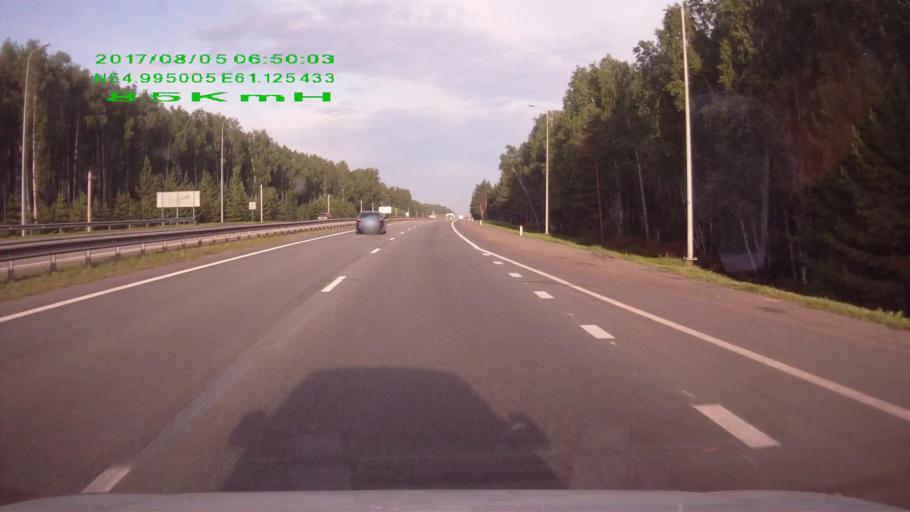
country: RU
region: Chelyabinsk
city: Poletayevo
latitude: 54.9949
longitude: 61.1250
